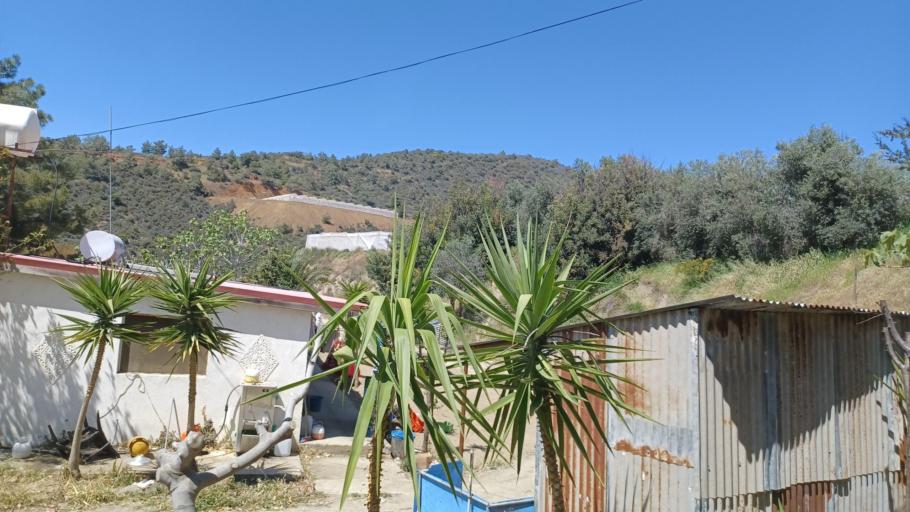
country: CY
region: Limassol
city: Parekklisha
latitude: 34.8159
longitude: 33.1442
